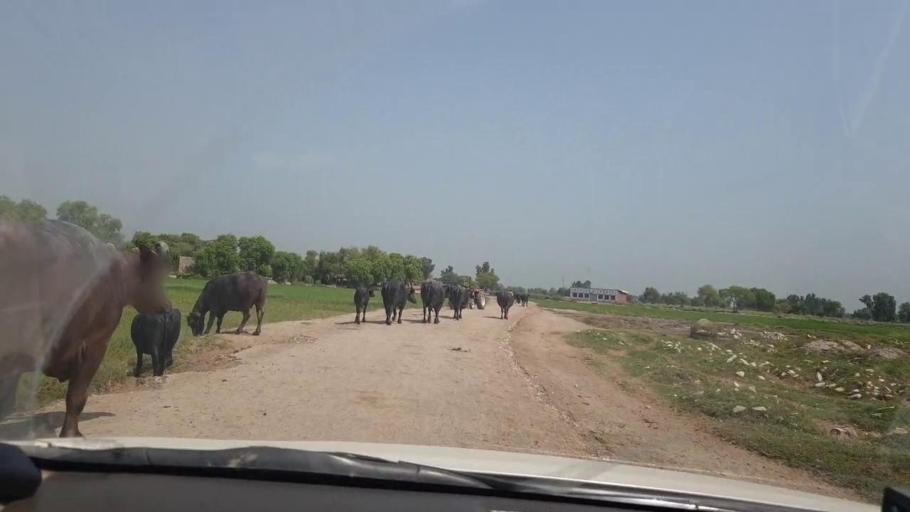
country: PK
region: Sindh
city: Chak
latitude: 27.8791
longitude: 68.7819
